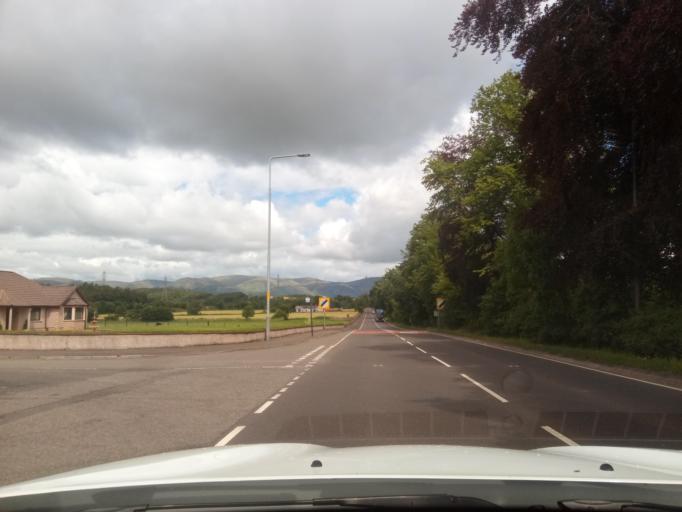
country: GB
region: Scotland
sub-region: Fife
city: Kincardine
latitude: 56.0797
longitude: -3.7202
